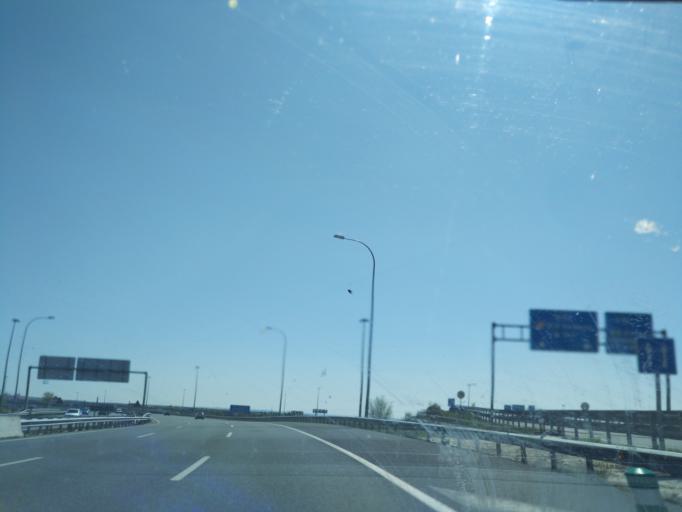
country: ES
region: Madrid
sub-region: Provincia de Madrid
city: Villa de Vallecas
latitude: 40.3618
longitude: -3.5706
